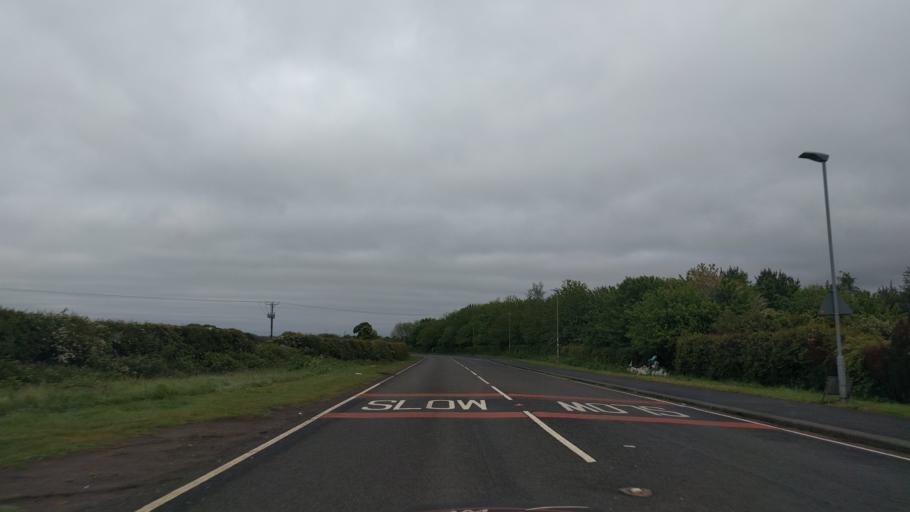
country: GB
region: England
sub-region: Northumberland
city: Choppington
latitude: 55.1609
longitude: -1.6240
